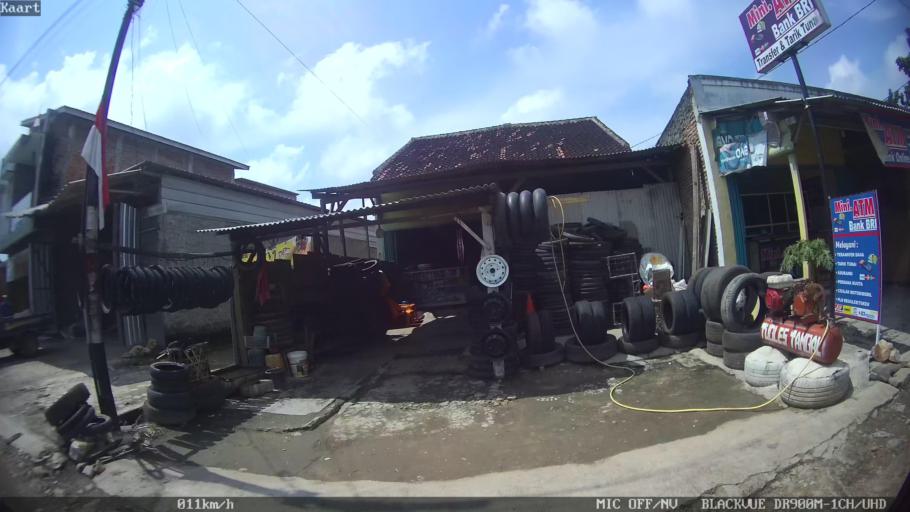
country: ID
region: Lampung
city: Kedaton
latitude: -5.3379
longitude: 105.2951
